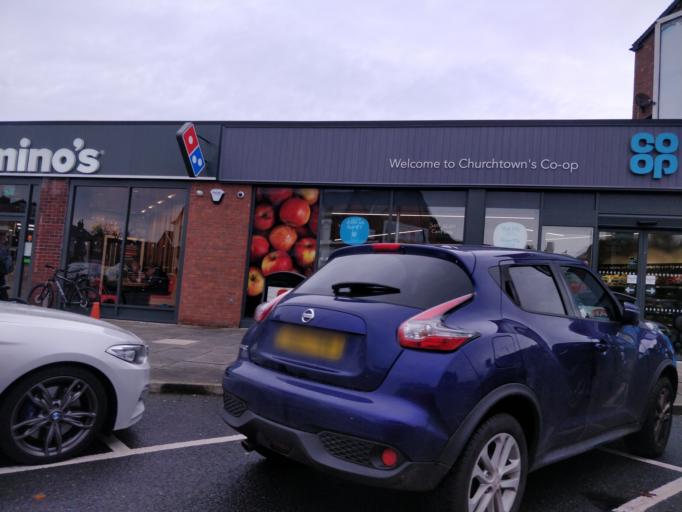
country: GB
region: England
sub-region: Sefton
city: Southport
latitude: 53.6614
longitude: -2.9659
